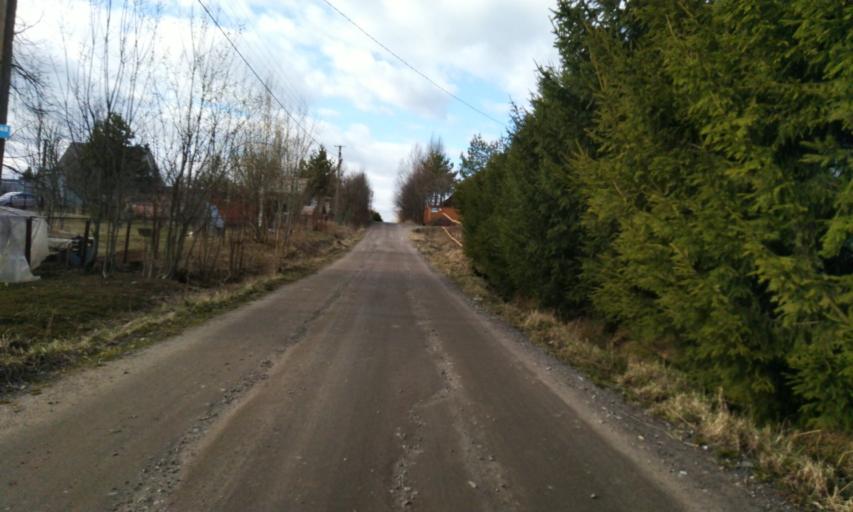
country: RU
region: Leningrad
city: Toksovo
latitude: 60.1282
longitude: 30.4893
